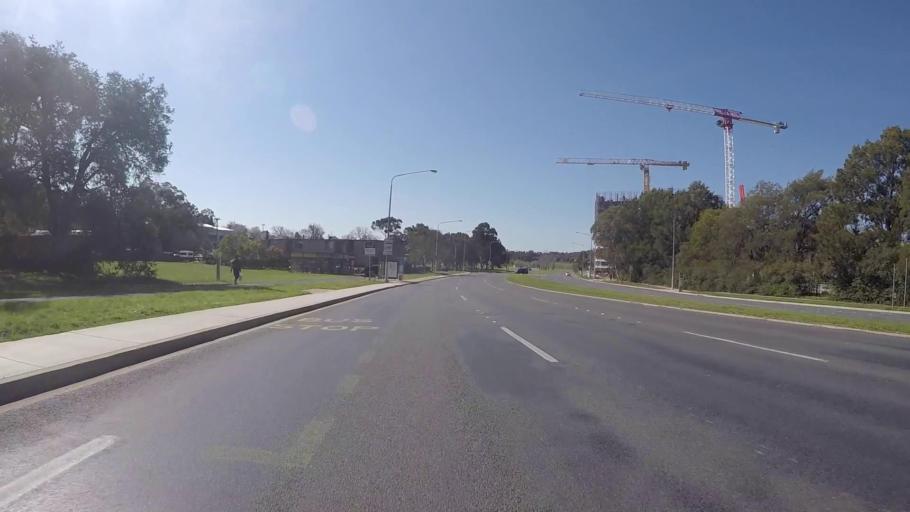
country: AU
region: Australian Capital Territory
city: Forrest
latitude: -35.3395
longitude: 149.0826
